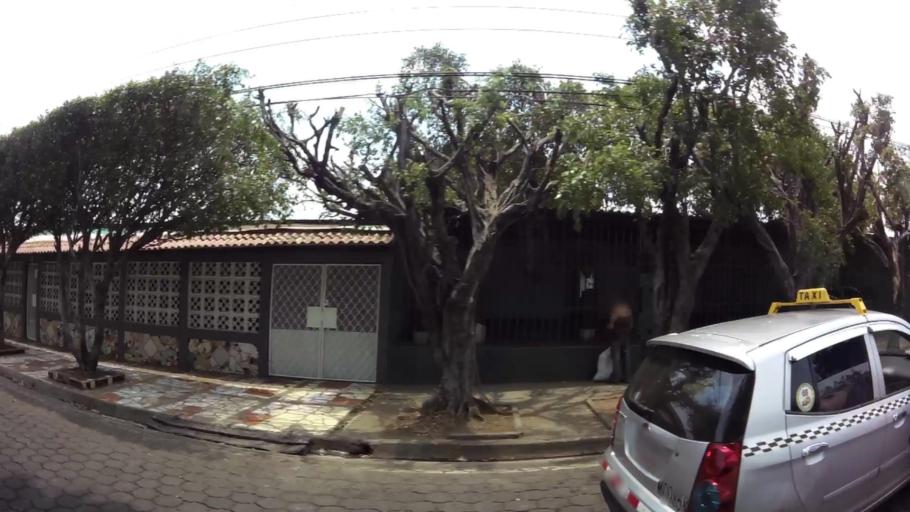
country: NI
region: Managua
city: Managua
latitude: 12.1229
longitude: -86.2973
